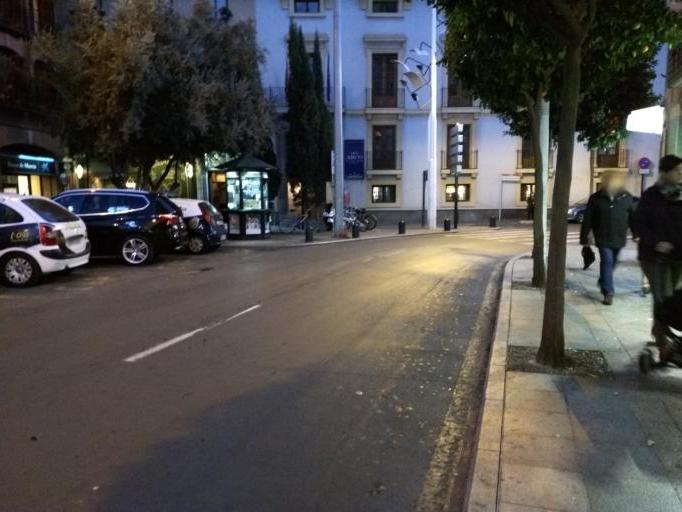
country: ES
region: Murcia
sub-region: Murcia
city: Murcia
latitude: 37.9835
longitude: -1.1269
